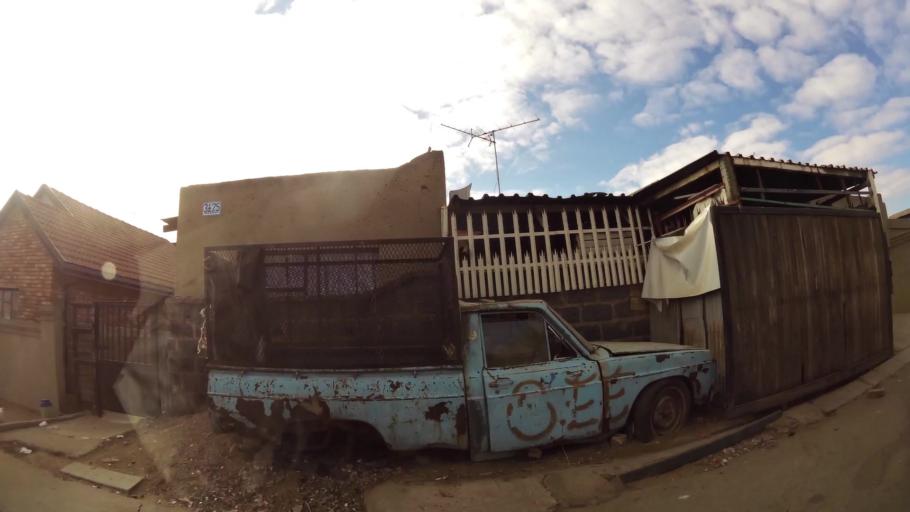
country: ZA
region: Gauteng
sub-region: City of Johannesburg Metropolitan Municipality
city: Modderfontein
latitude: -26.0377
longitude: 28.1841
